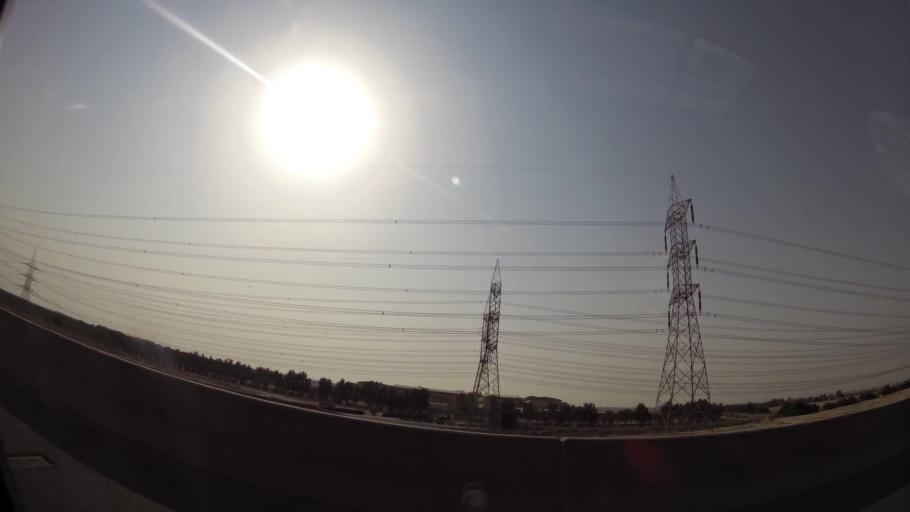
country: KW
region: Muhafazat al Jahra'
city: Al Jahra'
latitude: 29.3005
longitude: 47.7840
